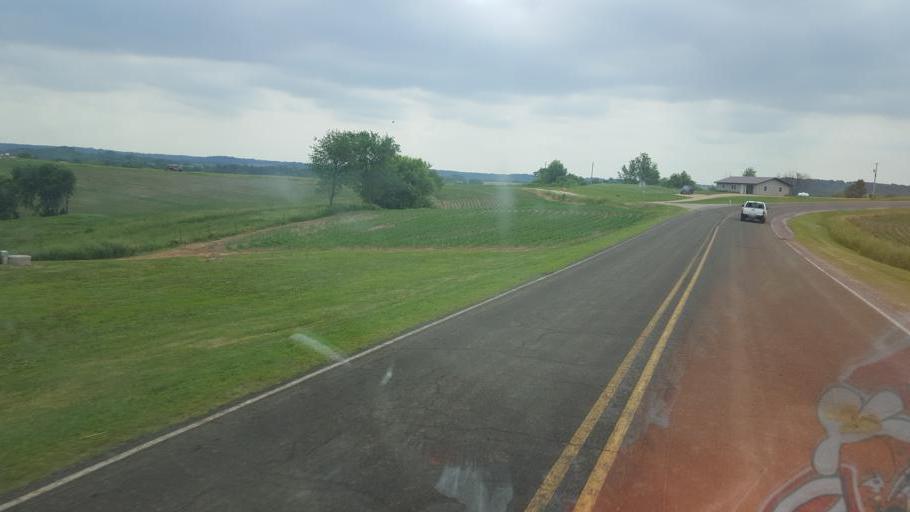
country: US
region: Wisconsin
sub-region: Vernon County
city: Hillsboro
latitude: 43.6452
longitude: -90.2705
